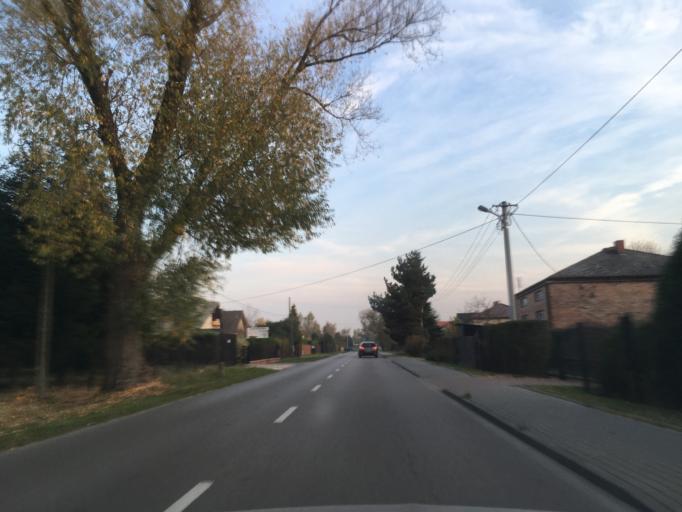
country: PL
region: Masovian Voivodeship
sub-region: Powiat piaseczynski
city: Lesznowola
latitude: 52.0541
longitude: 20.9256
